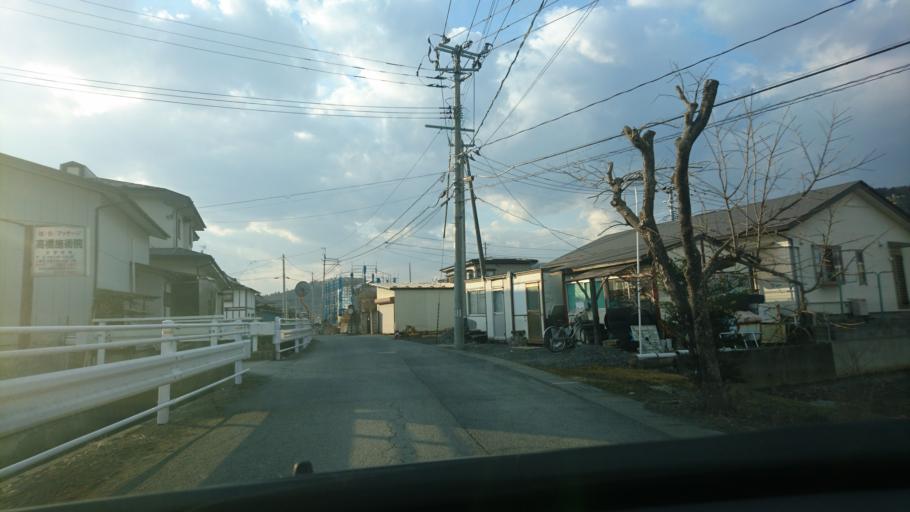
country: JP
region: Iwate
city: Ichinoseki
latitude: 38.9394
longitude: 141.0878
